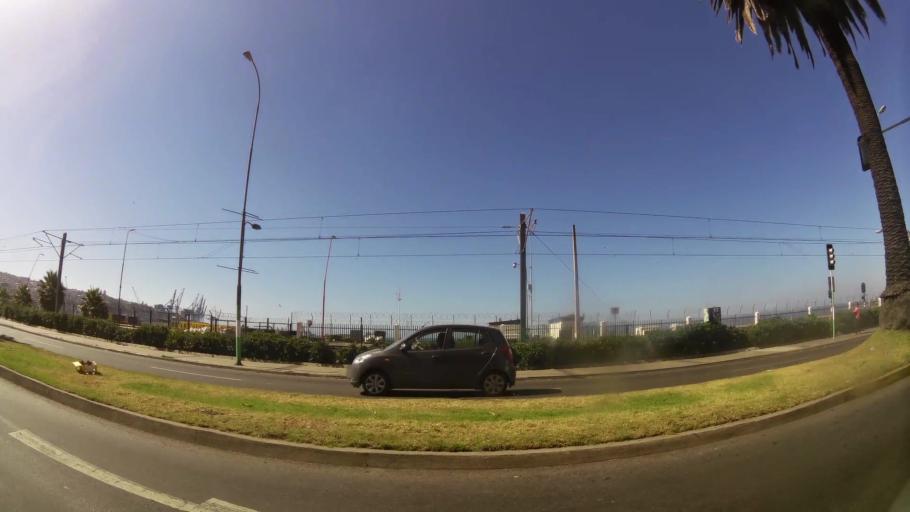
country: CL
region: Valparaiso
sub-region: Provincia de Valparaiso
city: Valparaiso
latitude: -33.0435
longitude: -71.6189
